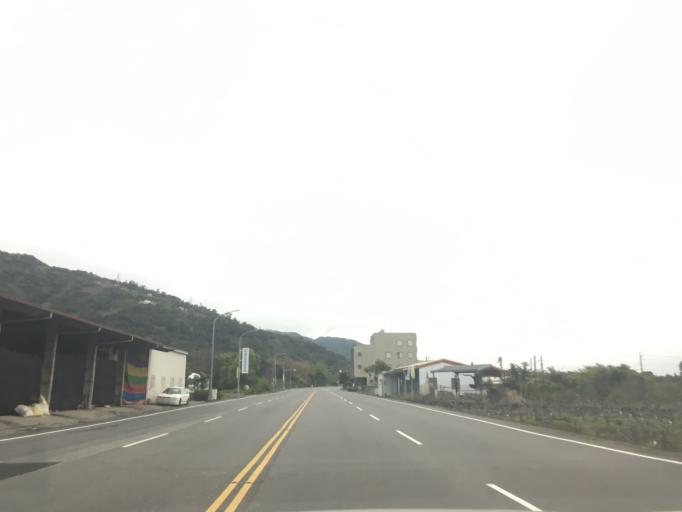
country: TW
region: Taiwan
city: Taitung City
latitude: 22.7285
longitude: 121.0562
